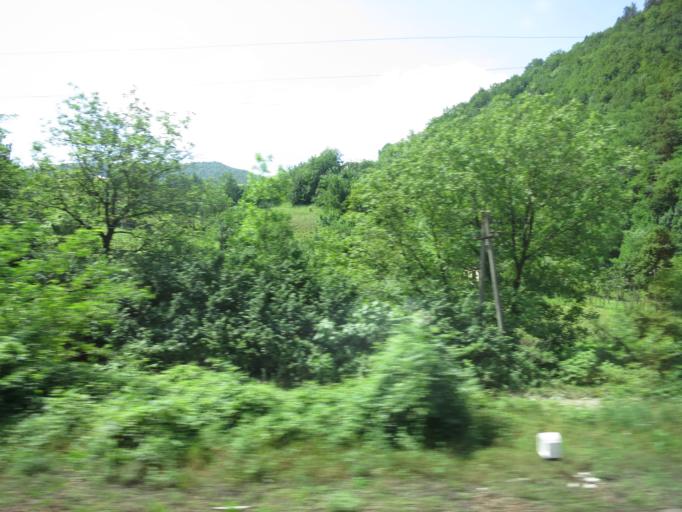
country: GE
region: Imereti
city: Kharagauli
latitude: 41.9990
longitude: 43.2280
